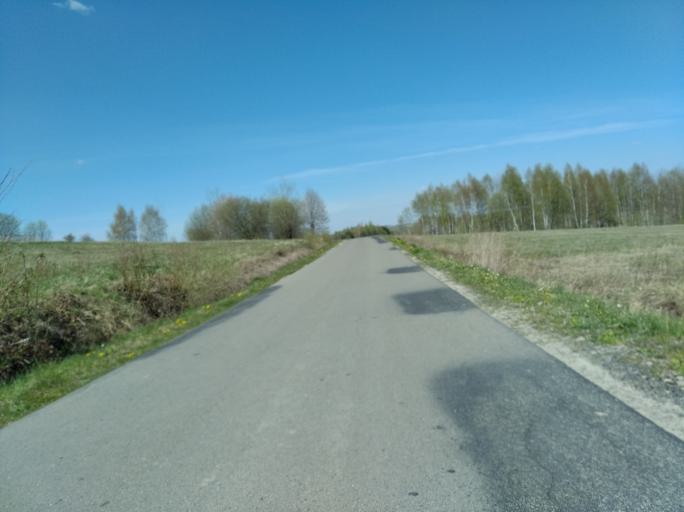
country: PL
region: Subcarpathian Voivodeship
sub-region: Powiat brzozowski
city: Jablonka
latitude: 49.7376
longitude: 22.1139
